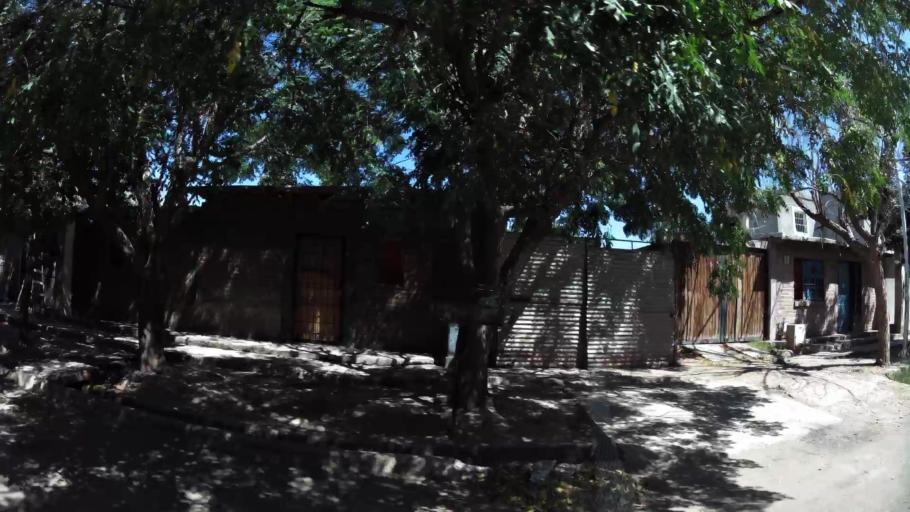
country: AR
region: Mendoza
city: Mendoza
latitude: -32.8760
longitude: -68.8063
